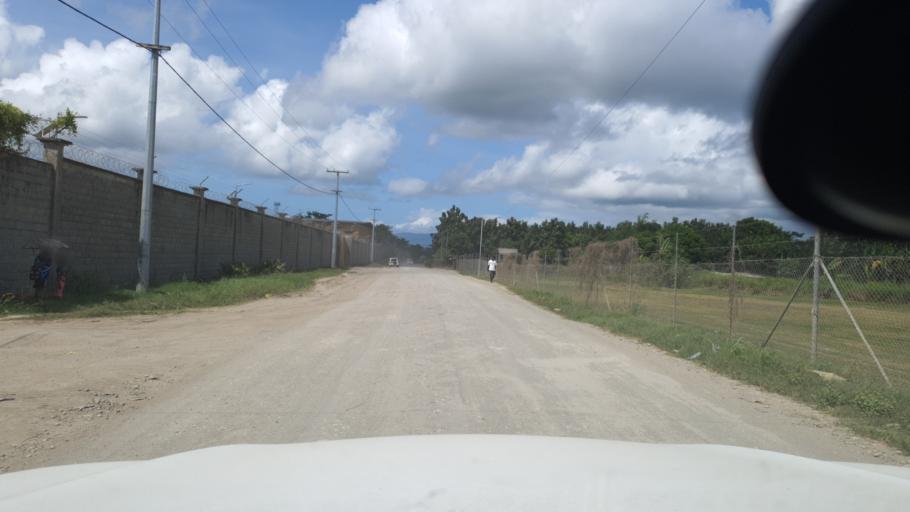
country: SB
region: Guadalcanal
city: Honiara
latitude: -9.4241
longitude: 160.0374
